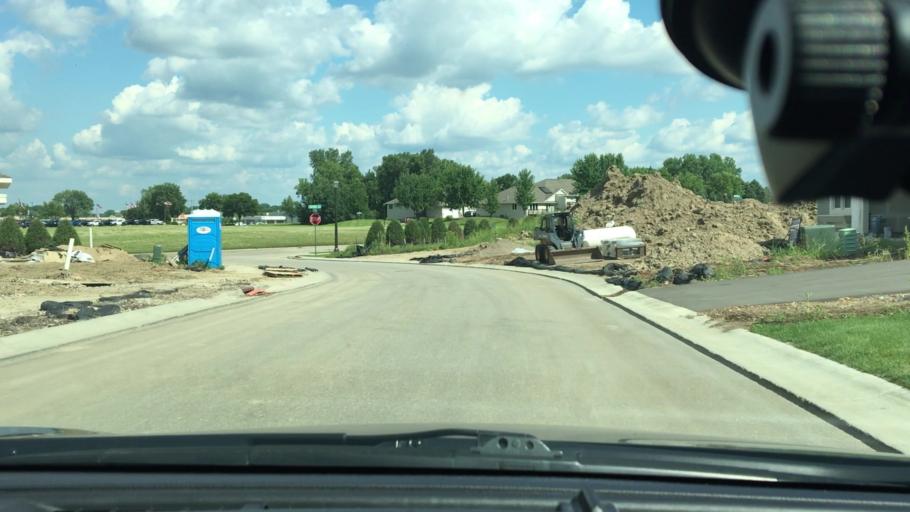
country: US
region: Minnesota
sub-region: Hennepin County
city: New Hope
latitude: 45.0562
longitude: -93.4091
